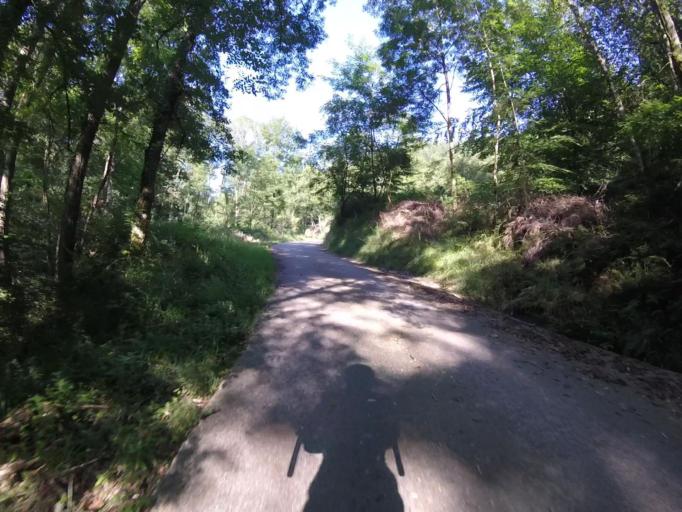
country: ES
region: Navarre
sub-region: Provincia de Navarra
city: Arano
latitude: 43.2451
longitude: -1.9078
